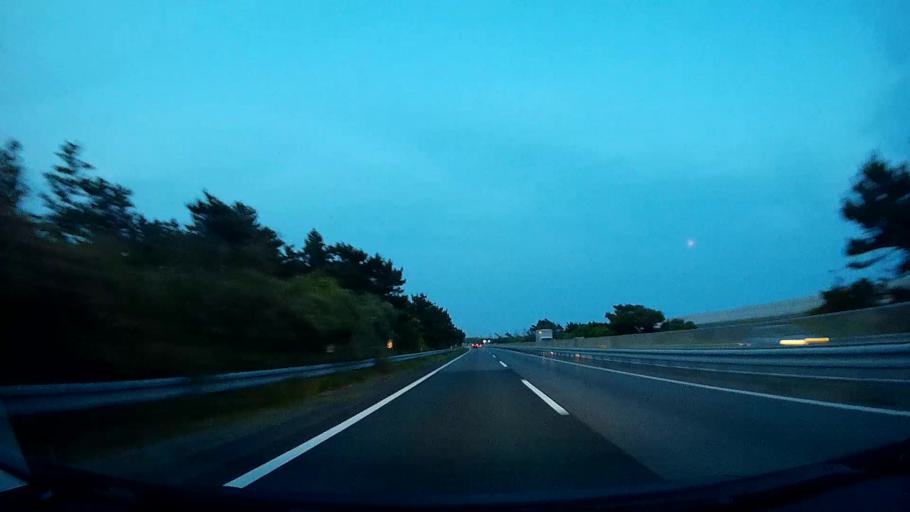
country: JP
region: Shizuoka
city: Hamamatsu
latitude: 34.6767
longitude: 137.6338
